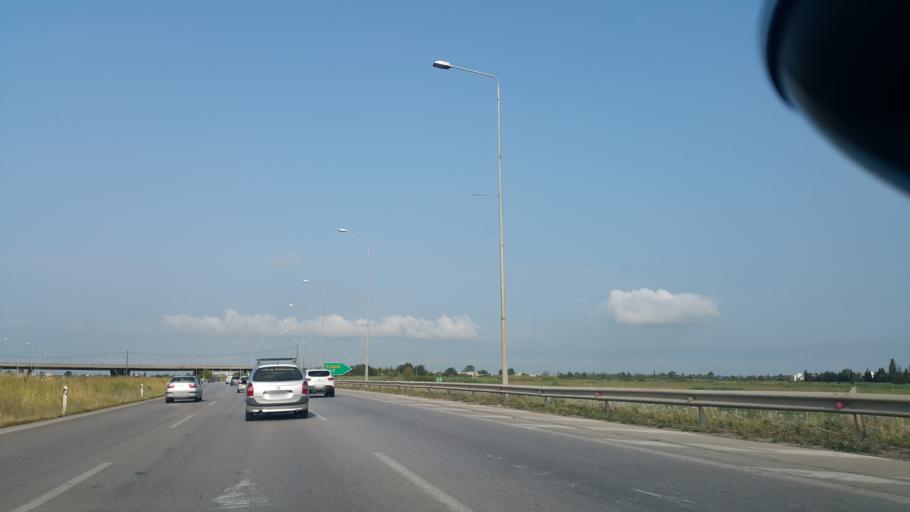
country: GR
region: Central Macedonia
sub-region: Nomos Thessalonikis
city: Sindos
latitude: 40.6510
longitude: 22.8168
